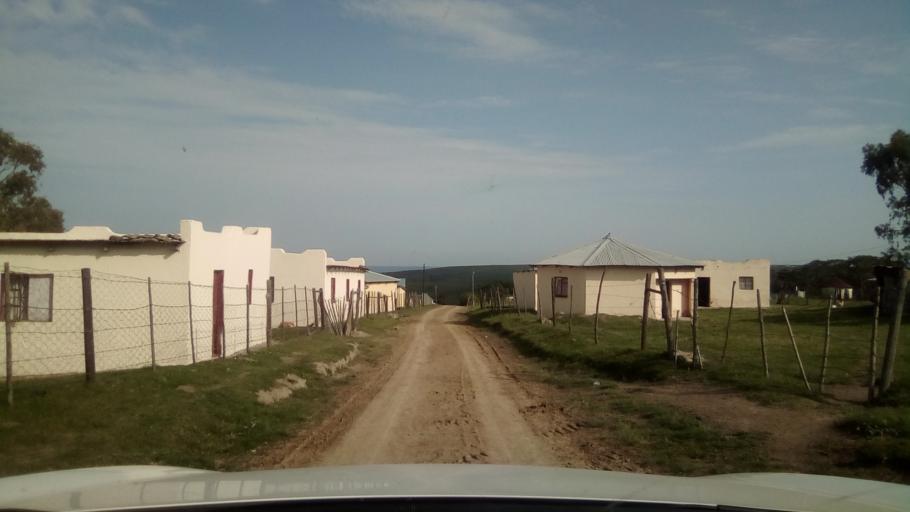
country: ZA
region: Eastern Cape
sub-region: Buffalo City Metropolitan Municipality
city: Bhisho
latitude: -33.0060
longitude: 27.3023
